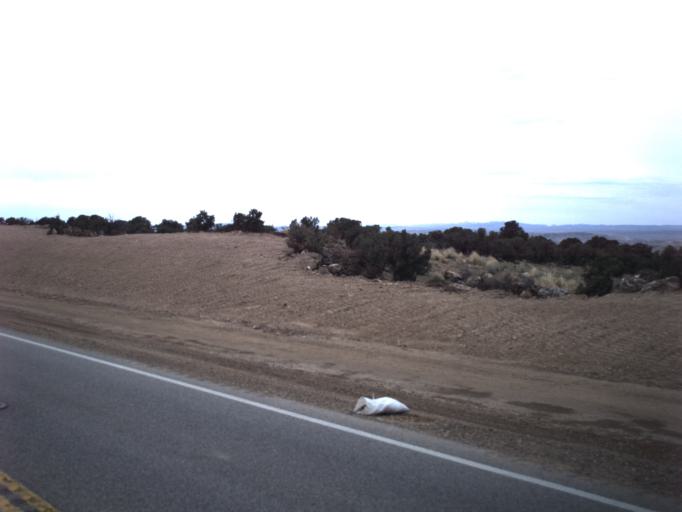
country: US
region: Utah
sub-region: Carbon County
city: East Carbon City
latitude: 39.4011
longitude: -110.4237
